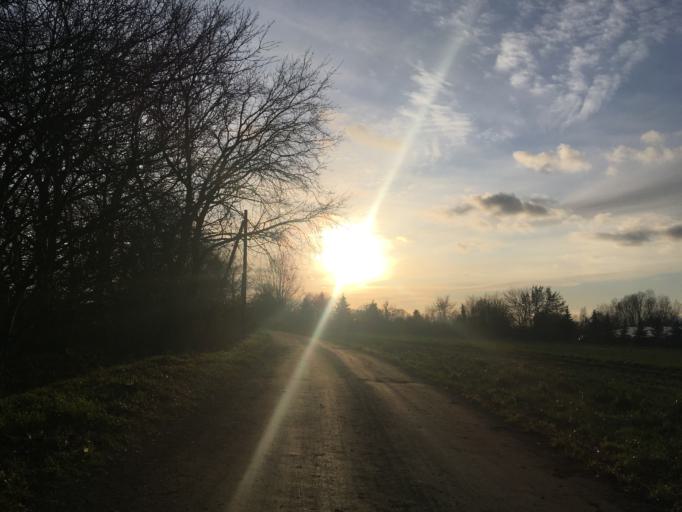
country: DE
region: Berlin
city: Buchholz
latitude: 52.6223
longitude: 13.4218
